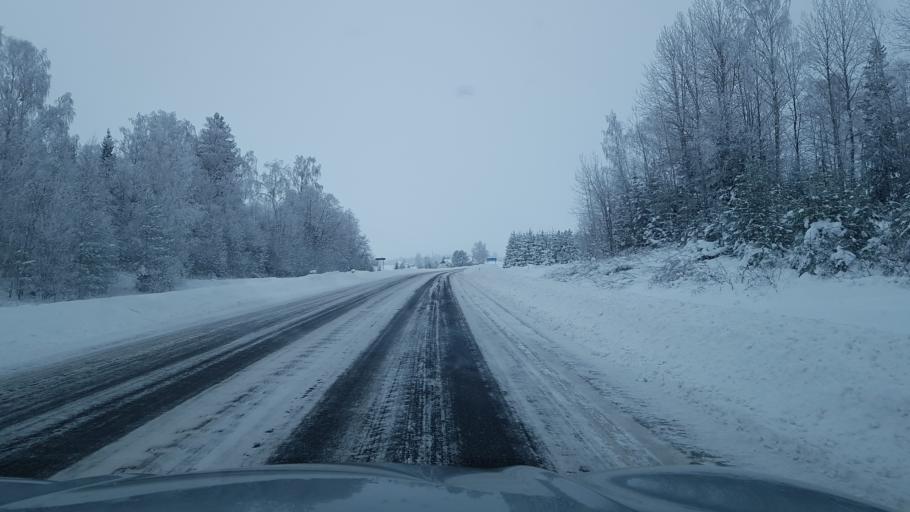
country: EE
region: Ida-Virumaa
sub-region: Johvi vald
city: Johvi
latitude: 59.2338
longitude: 27.3448
